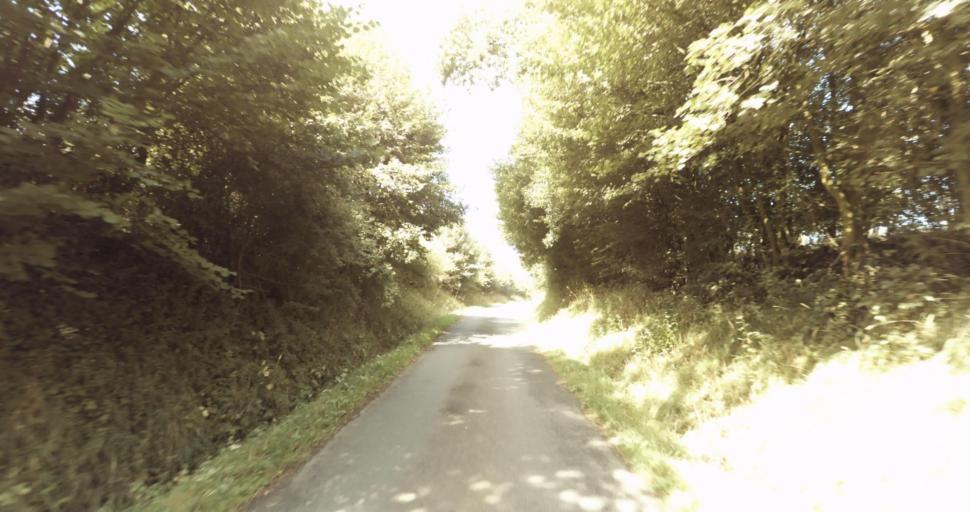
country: FR
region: Lower Normandy
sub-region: Departement du Calvados
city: Orbec
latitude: 48.9132
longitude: 0.3827
